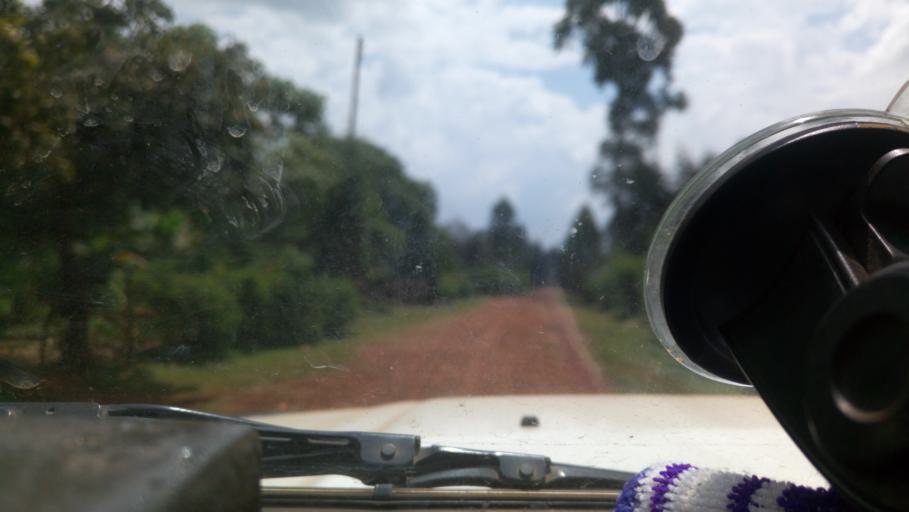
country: KE
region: Kericho
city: Litein
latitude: -0.5932
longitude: 35.1535
